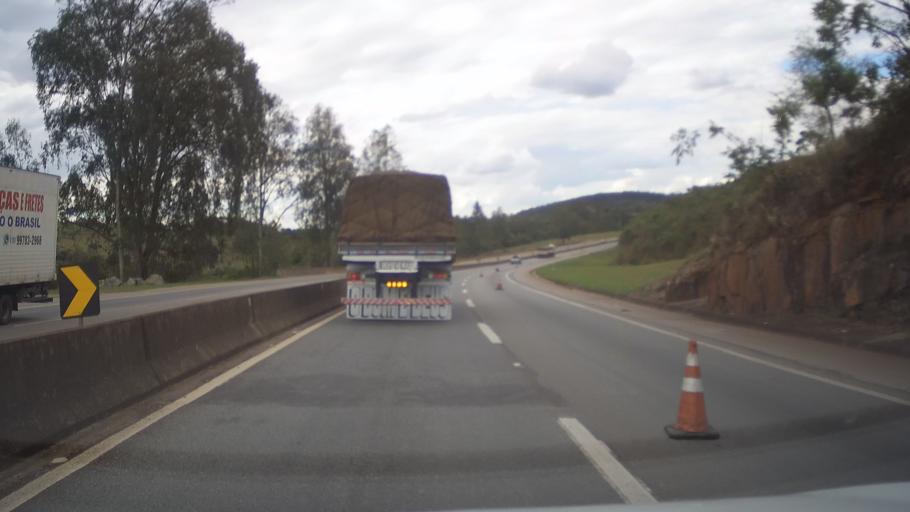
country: BR
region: Minas Gerais
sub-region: Itauna
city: Itauna
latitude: -20.3258
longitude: -44.4565
